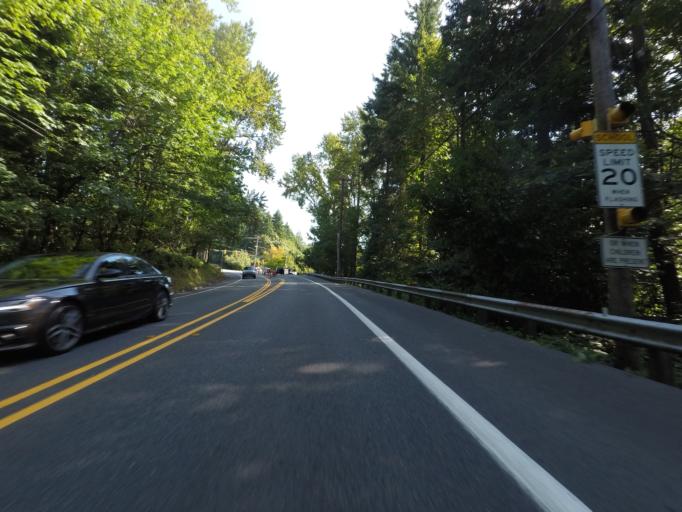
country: US
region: Washington
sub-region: King County
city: Kenmore
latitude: 47.7390
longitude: -122.2506
